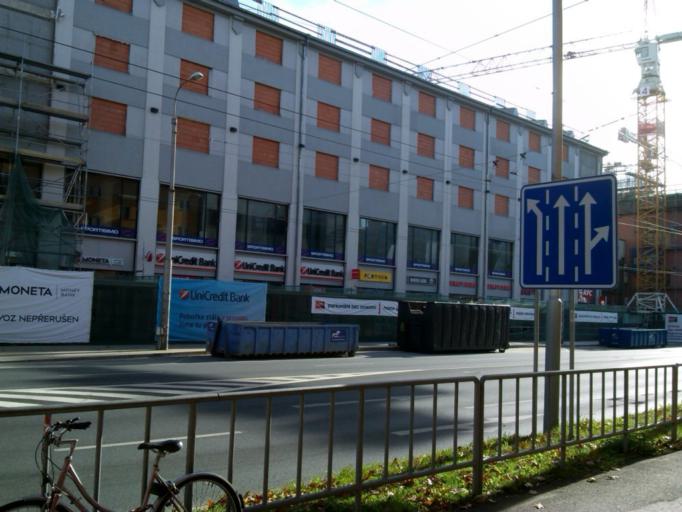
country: CZ
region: Jihocesky
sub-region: Okres Ceske Budejovice
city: Ceske Budejovice
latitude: 48.9848
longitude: 14.4715
